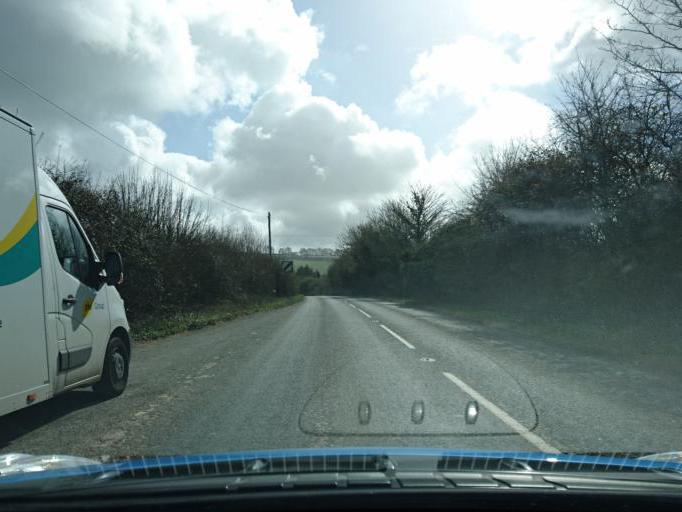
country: GB
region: England
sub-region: South Gloucestershire
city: Pucklechurch
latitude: 51.4512
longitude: -2.4115
